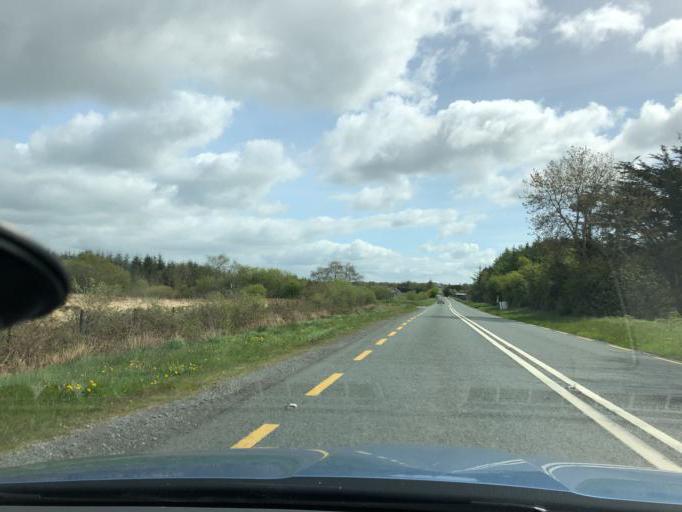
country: IE
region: Munster
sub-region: County Cork
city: Millstreet
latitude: 52.0715
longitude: -9.2759
